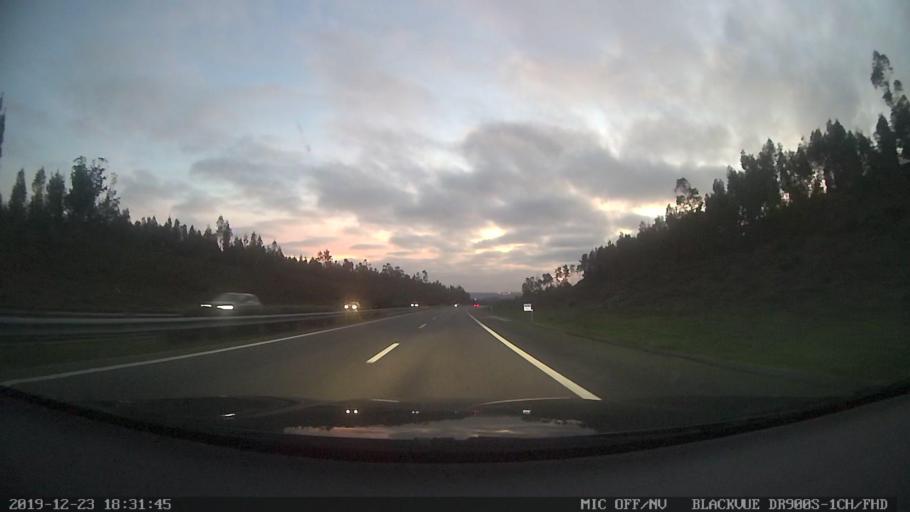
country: PT
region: Coimbra
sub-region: Soure
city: Soure
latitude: 39.9927
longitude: -8.6182
